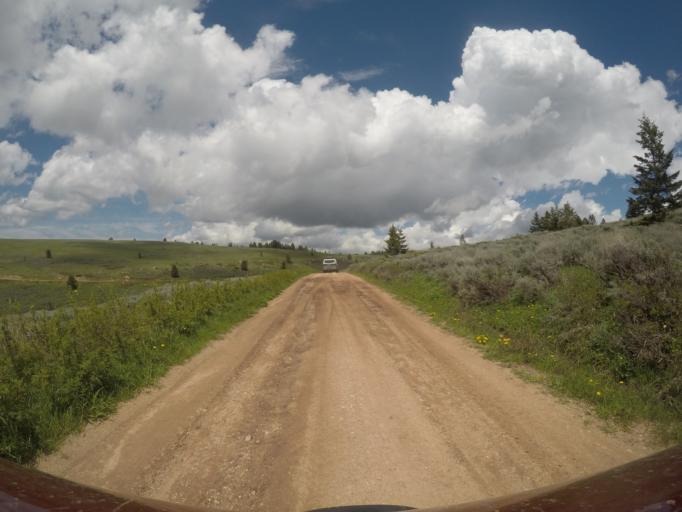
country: US
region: Wyoming
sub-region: Big Horn County
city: Lovell
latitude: 45.1791
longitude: -108.4370
